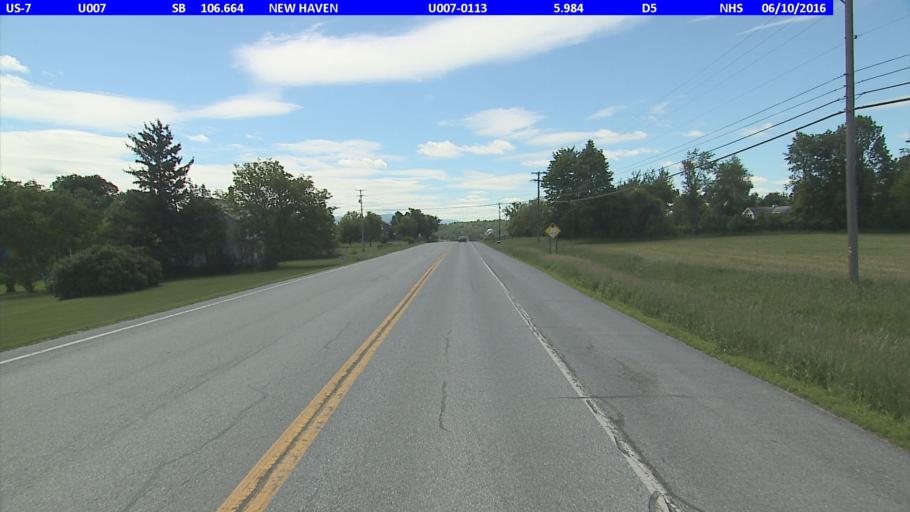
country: US
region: Vermont
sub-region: Addison County
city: Vergennes
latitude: 44.1297
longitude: -73.1886
